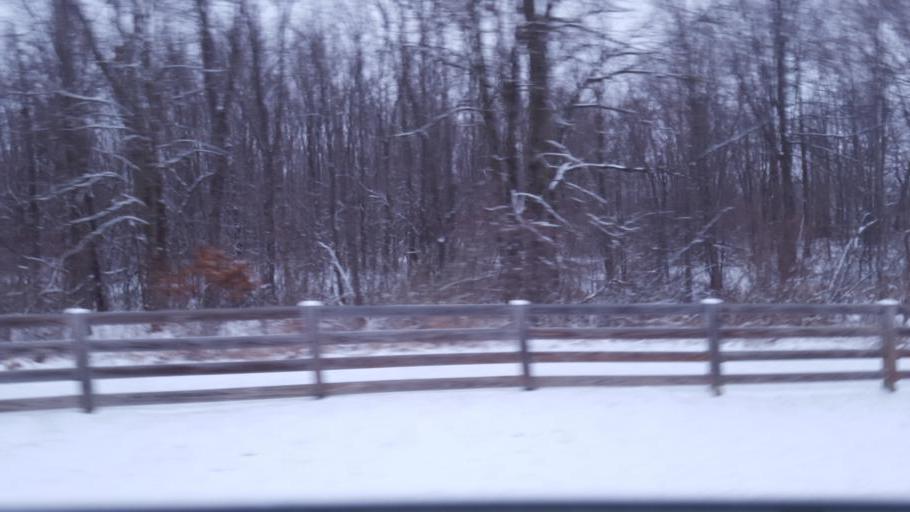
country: US
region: Ohio
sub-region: Morrow County
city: Mount Gilead
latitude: 40.5150
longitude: -82.7629
